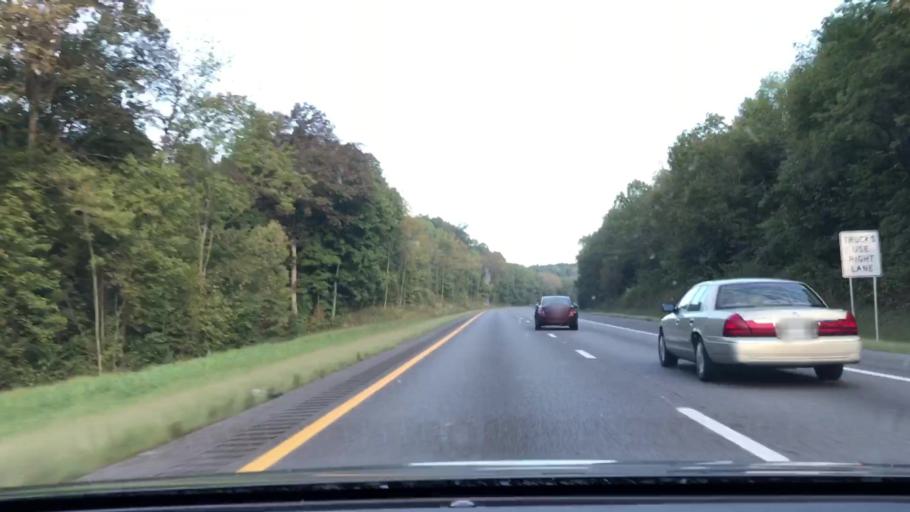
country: US
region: Tennessee
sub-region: Montgomery County
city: Clarksville
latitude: 36.5463
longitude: -87.2405
